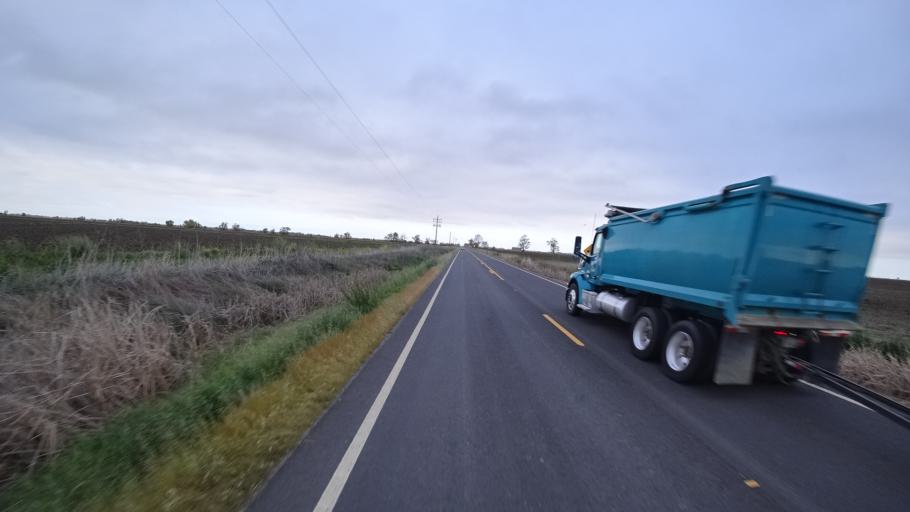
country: US
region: California
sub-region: Glenn County
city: Willows
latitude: 39.4064
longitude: -122.0757
